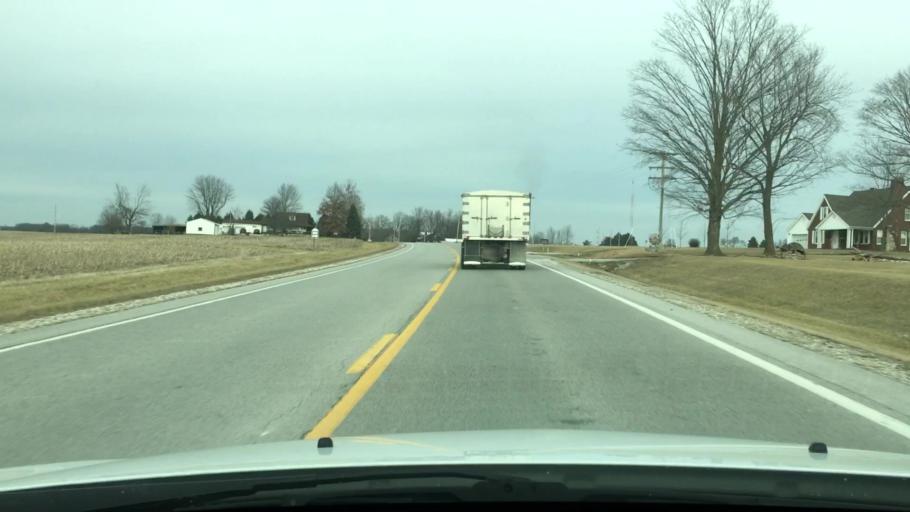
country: US
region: Illinois
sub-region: Pike County
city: Pittsfield
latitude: 39.6449
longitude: -90.7848
